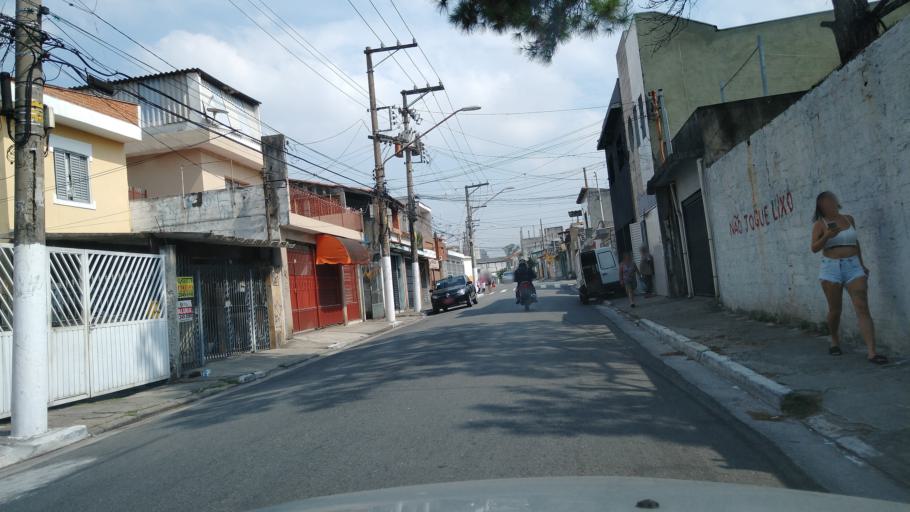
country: BR
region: Sao Paulo
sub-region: Guarulhos
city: Guarulhos
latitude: -23.4756
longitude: -46.5803
